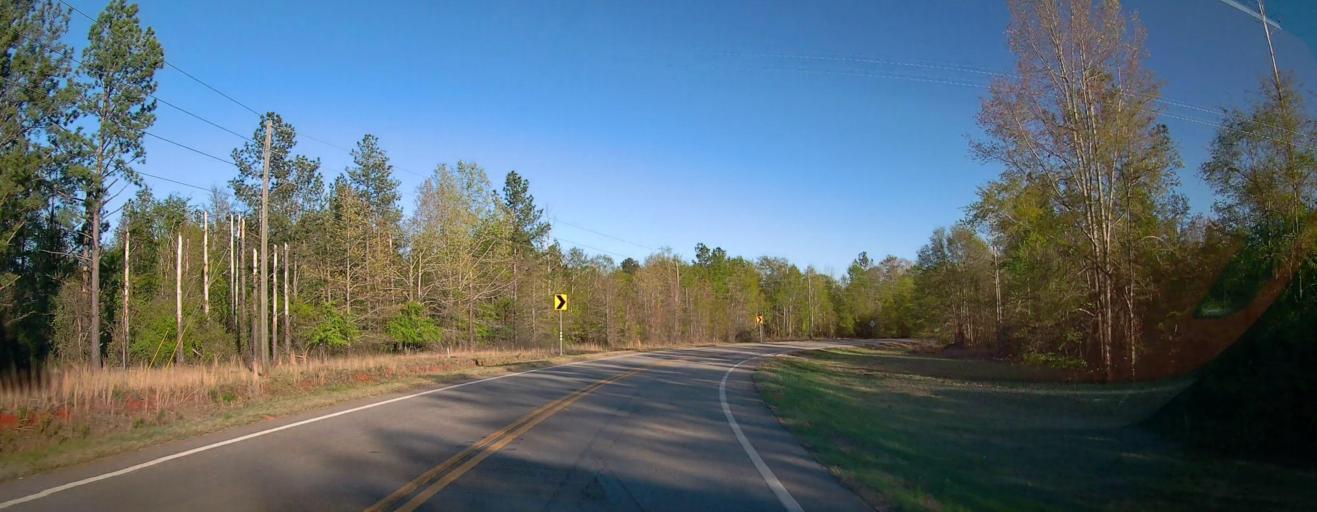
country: US
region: Georgia
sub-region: Wilkinson County
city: Irwinton
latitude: 32.8749
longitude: -83.0979
